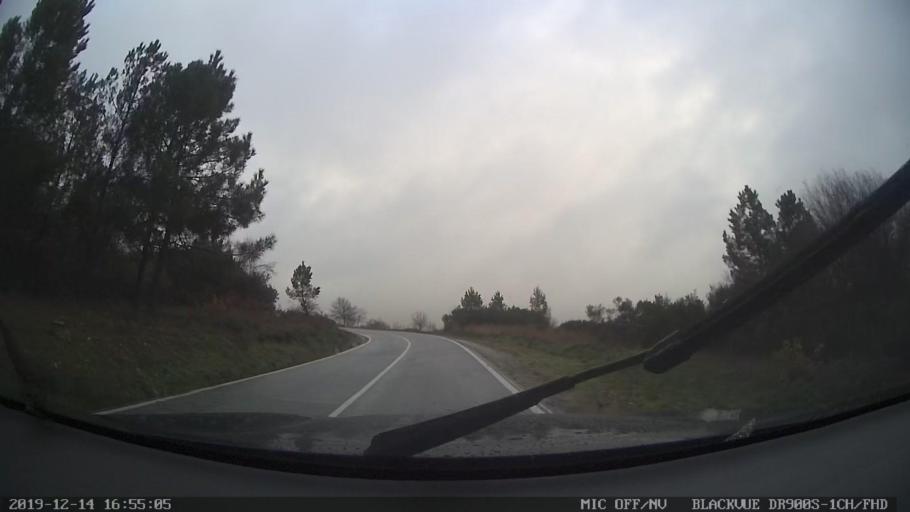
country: PT
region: Vila Real
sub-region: Murca
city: Murca
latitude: 41.4388
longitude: -7.5282
